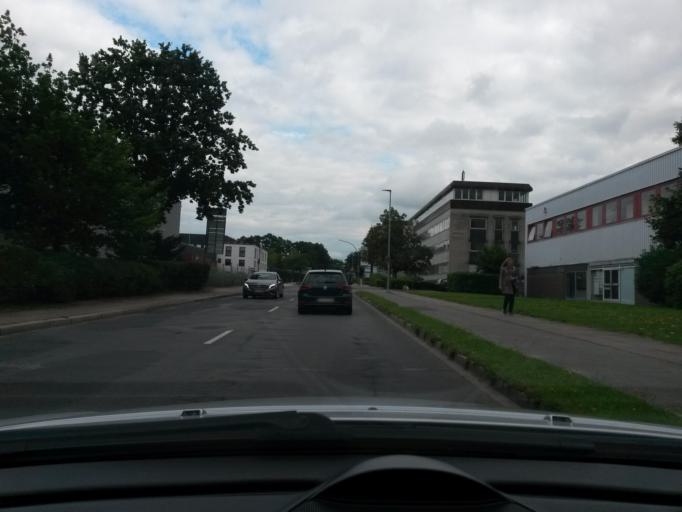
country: DE
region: Schleswig-Holstein
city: Reinbek
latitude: 53.5241
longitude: 10.2360
